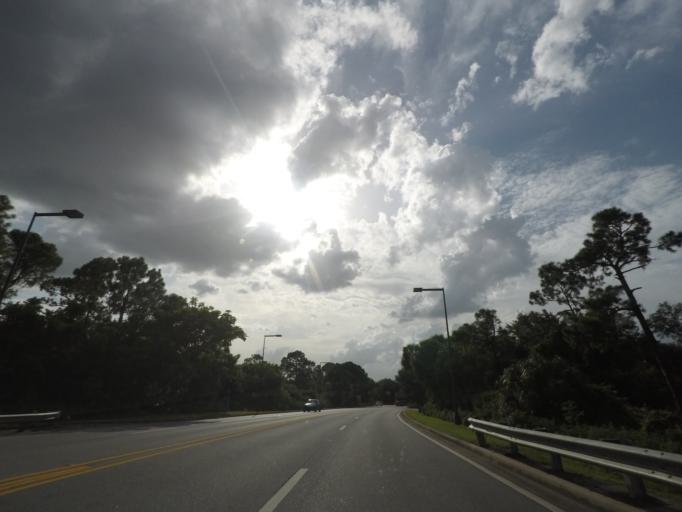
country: US
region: Florida
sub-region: Polk County
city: Citrus Ridge
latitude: 28.3513
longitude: -81.5981
